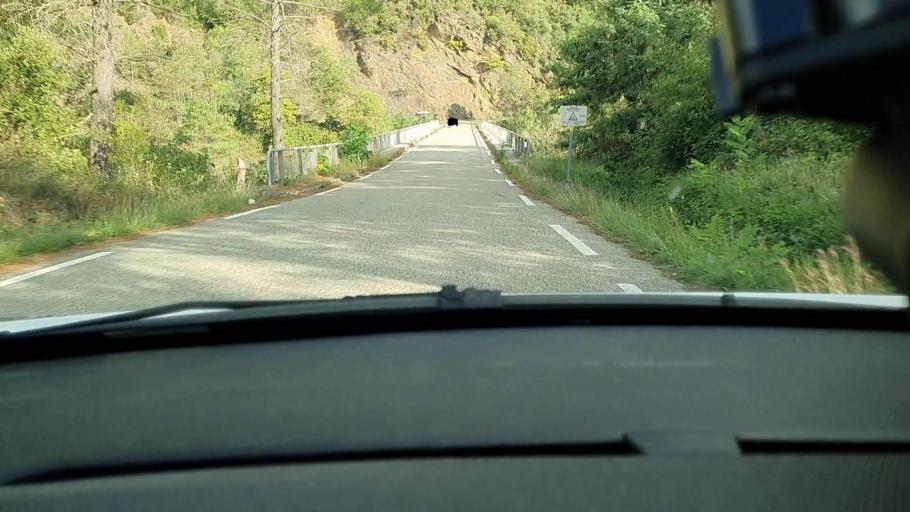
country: FR
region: Languedoc-Roussillon
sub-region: Departement du Gard
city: Besseges
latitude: 44.3185
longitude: 4.0379
